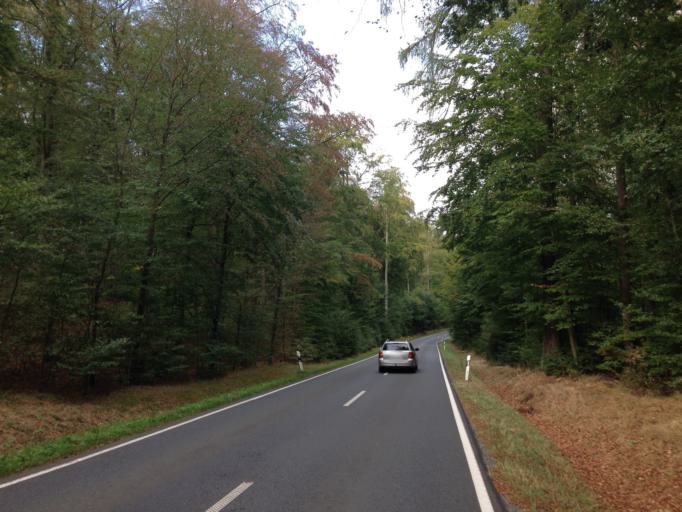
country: DE
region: Hesse
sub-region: Regierungsbezirk Giessen
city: Bad Endbach
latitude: 50.6736
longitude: 8.5440
